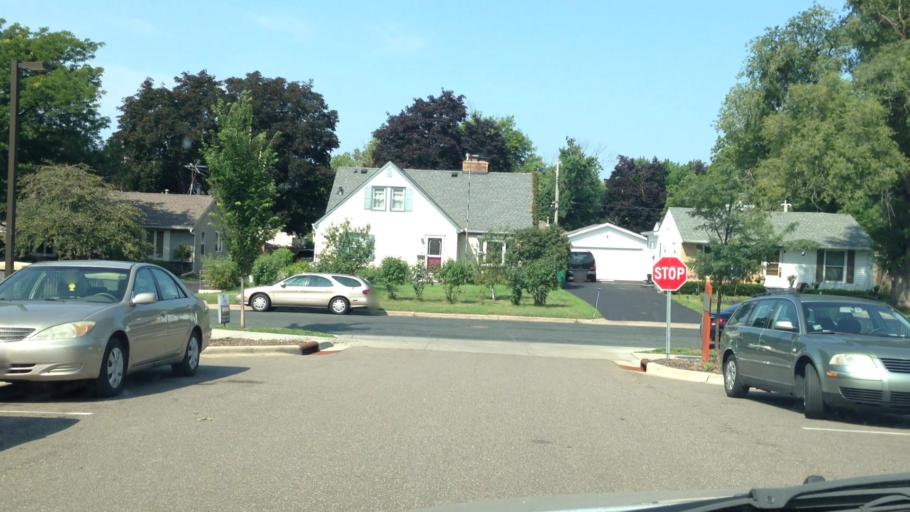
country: US
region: Minnesota
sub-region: Hennepin County
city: Saint Louis Park
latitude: 44.9627
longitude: -93.3669
